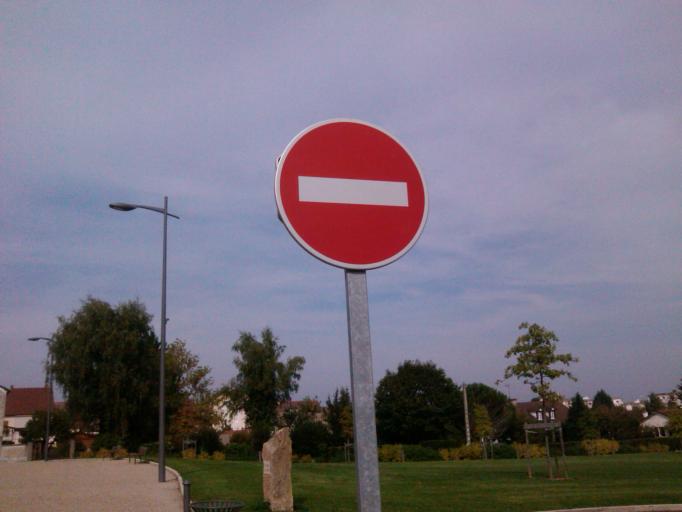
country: FR
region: Bourgogne
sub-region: Departement de Saone-et-Loire
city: Chatenoy-le-Royal
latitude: 46.7936
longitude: 4.8118
